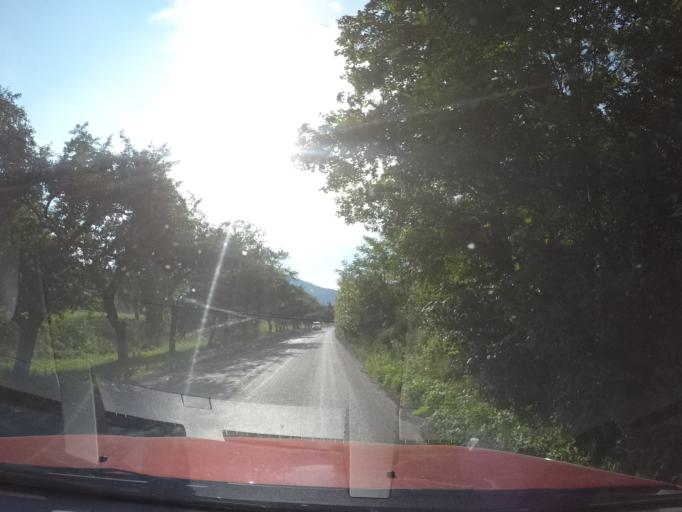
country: UA
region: Zakarpattia
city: Velykyi Bereznyi
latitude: 48.9515
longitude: 22.5374
